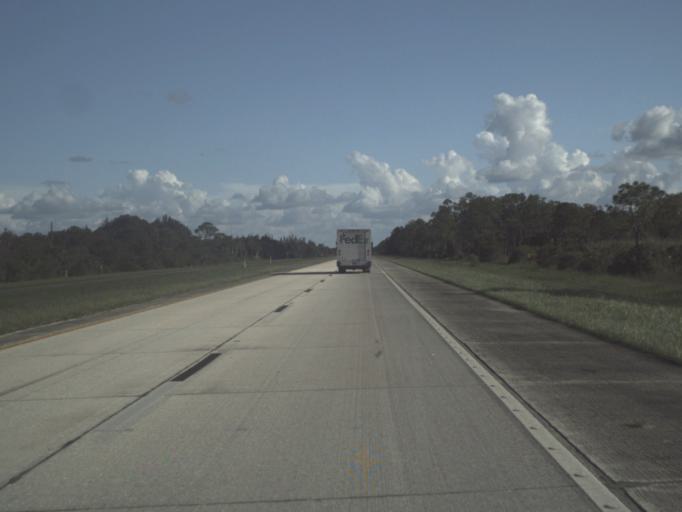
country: US
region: Florida
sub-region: Lee County
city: Burnt Store Marina
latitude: 26.8173
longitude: -81.9617
